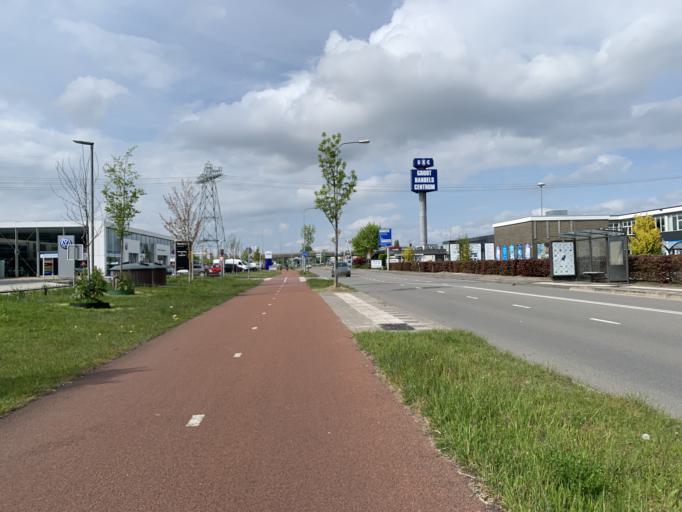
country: NL
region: Groningen
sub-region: Gemeente Groningen
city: Oosterpark
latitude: 53.2109
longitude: 6.5955
